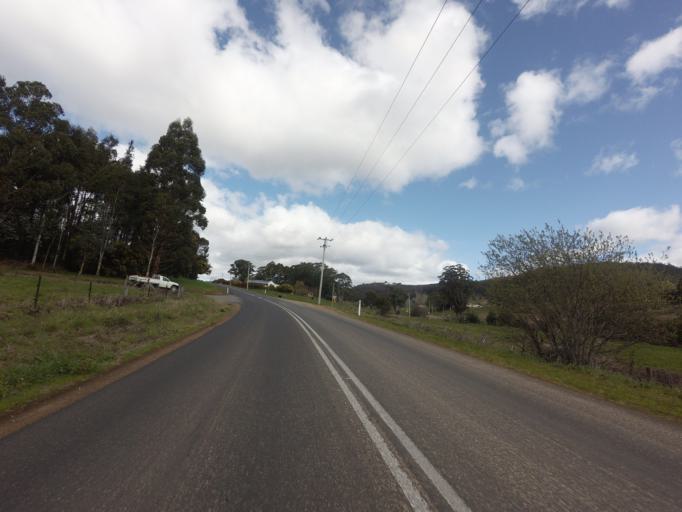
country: AU
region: Tasmania
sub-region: Huon Valley
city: Geeveston
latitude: -43.1774
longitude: 146.9241
